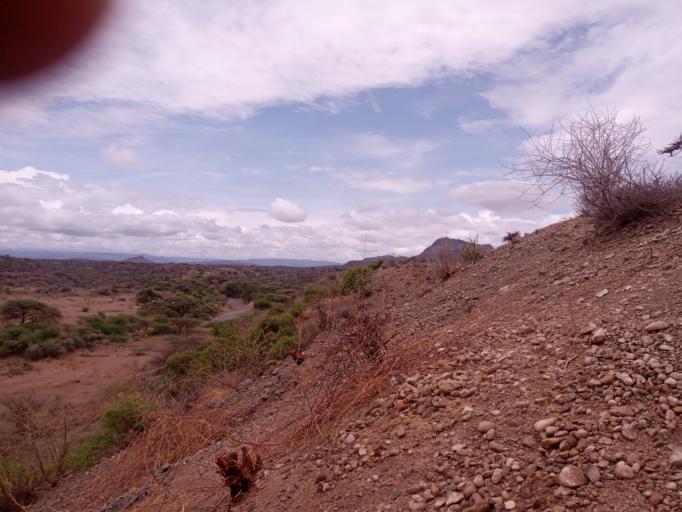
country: ET
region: Afar
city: Awash
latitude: 9.0305
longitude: 40.2107
